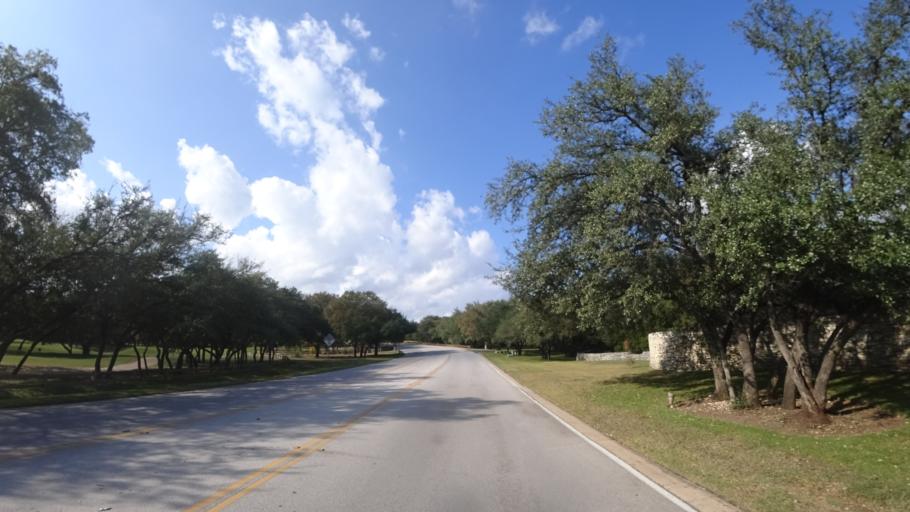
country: US
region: Texas
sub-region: Travis County
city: Lost Creek
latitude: 30.2966
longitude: -97.8543
